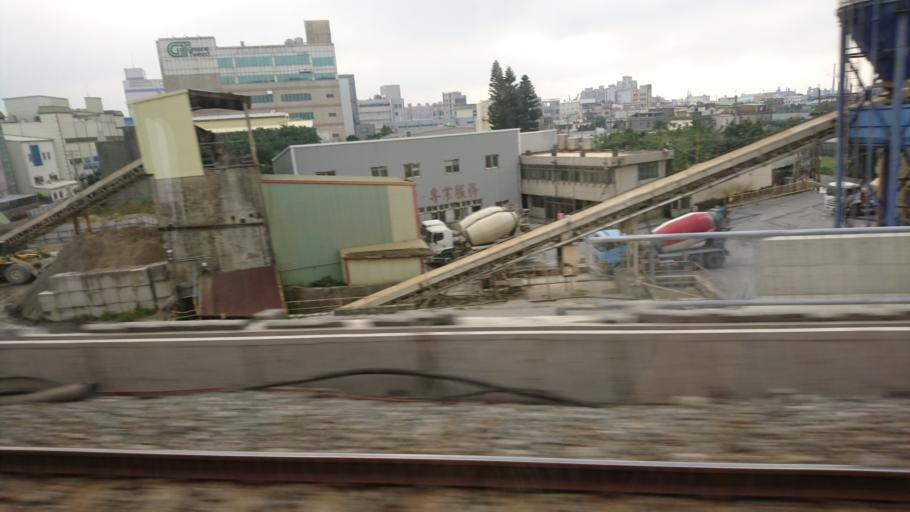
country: TW
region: Taiwan
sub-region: Hsinchu
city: Zhubei
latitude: 24.8499
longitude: 121.0136
